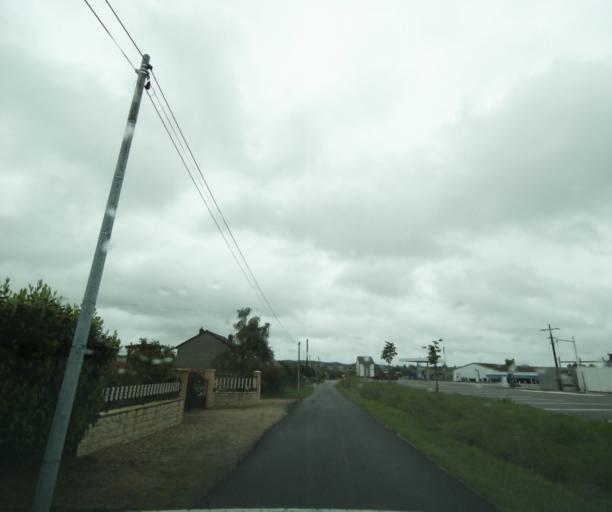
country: FR
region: Bourgogne
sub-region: Departement de Saone-et-Loire
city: Charolles
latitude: 46.4810
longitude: 4.4306
